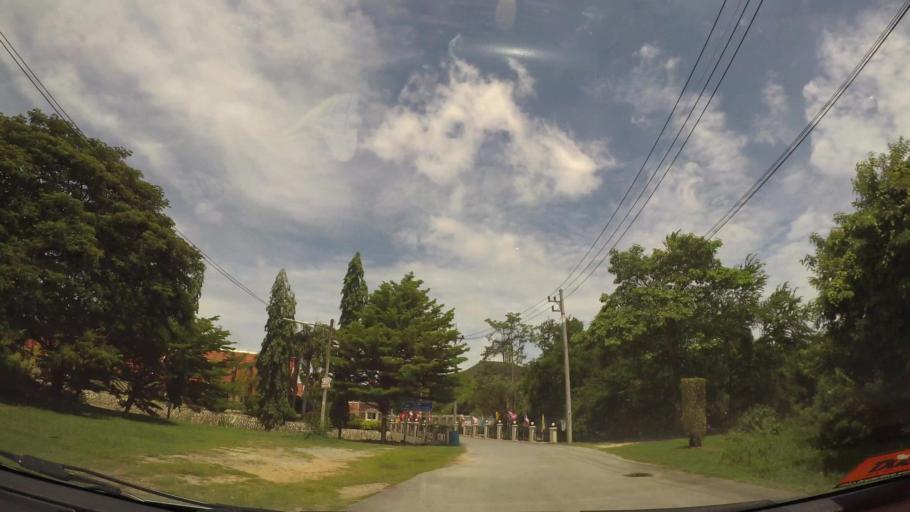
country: TH
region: Chon Buri
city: Sattahip
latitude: 12.7421
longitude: 100.8898
